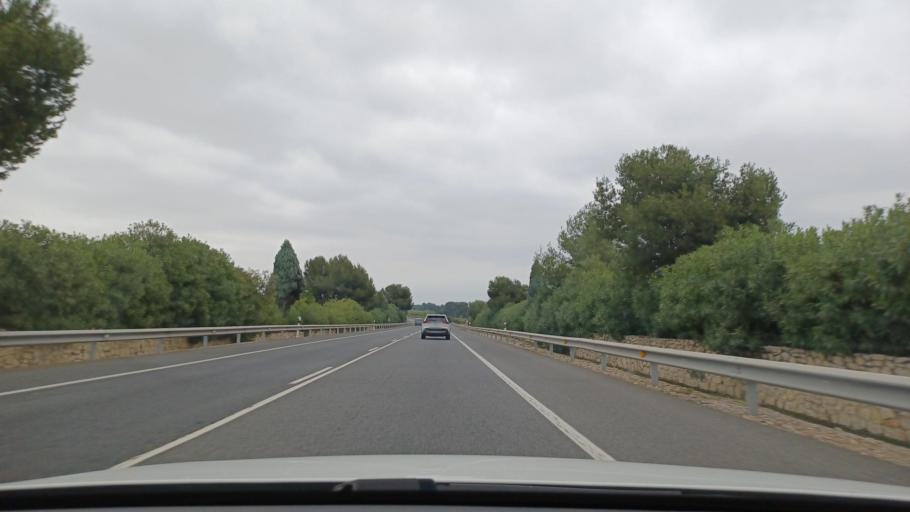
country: ES
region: Valencia
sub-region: Provincia de Castello
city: Borriol
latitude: 40.0044
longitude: -0.0660
